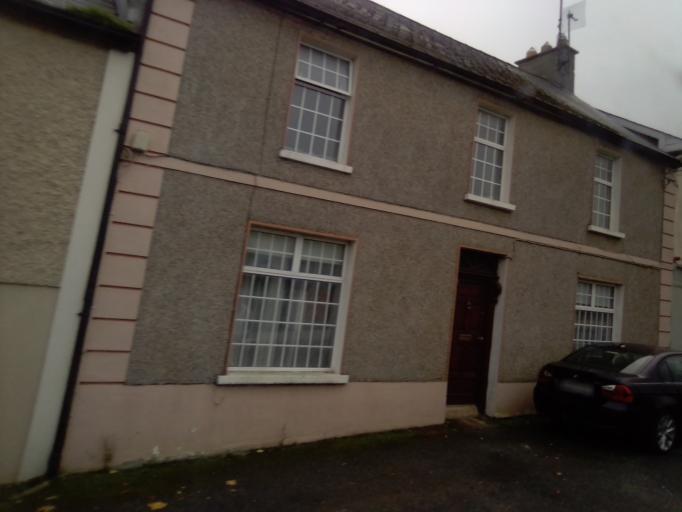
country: IE
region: Leinster
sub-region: Uibh Fhaili
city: Birr
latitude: 52.9842
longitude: -7.9248
